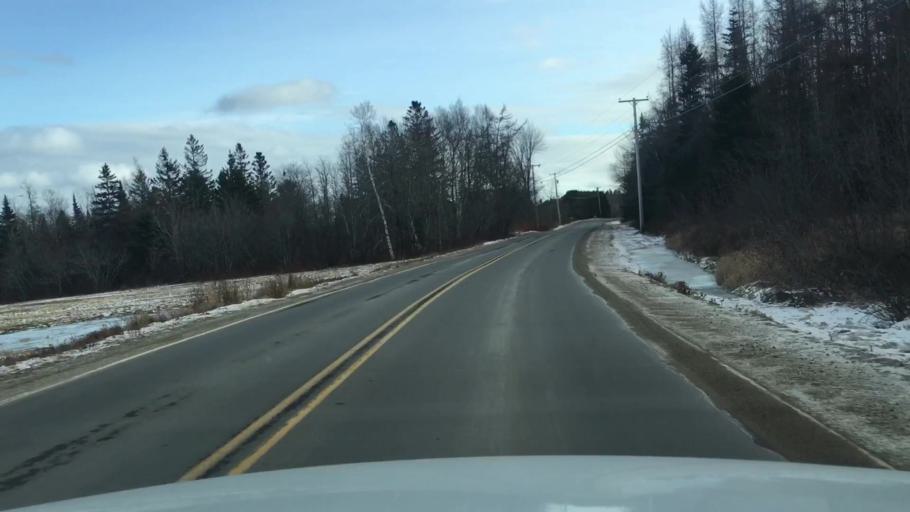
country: US
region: Maine
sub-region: Washington County
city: Jonesport
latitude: 44.6151
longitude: -67.6044
